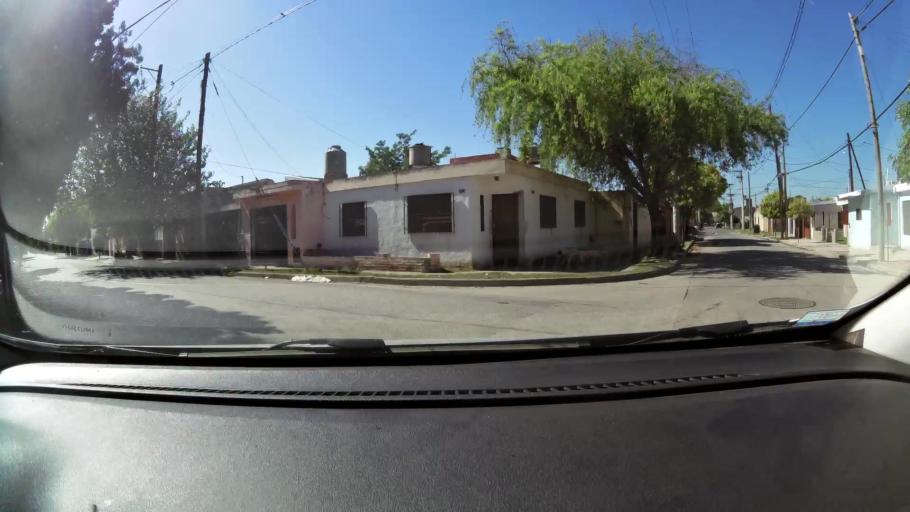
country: AR
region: Cordoba
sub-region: Departamento de Capital
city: Cordoba
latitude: -31.4425
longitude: -64.1420
